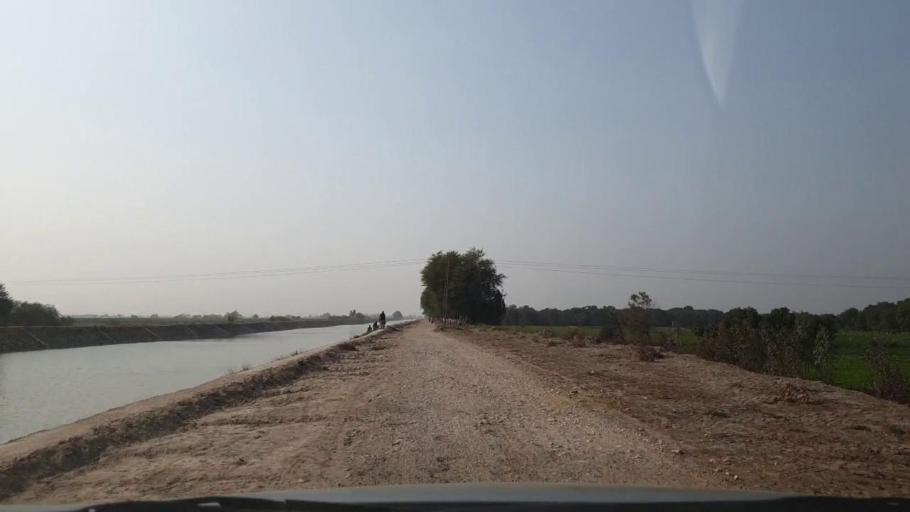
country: PK
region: Sindh
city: Tando Adam
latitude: 25.6393
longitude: 68.5900
